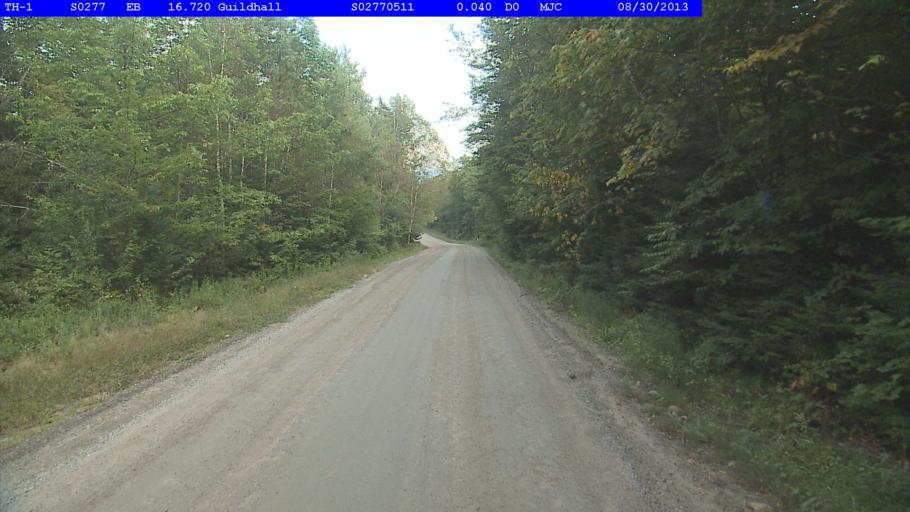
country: US
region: Vermont
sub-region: Essex County
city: Guildhall
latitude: 44.5743
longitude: -71.6689
